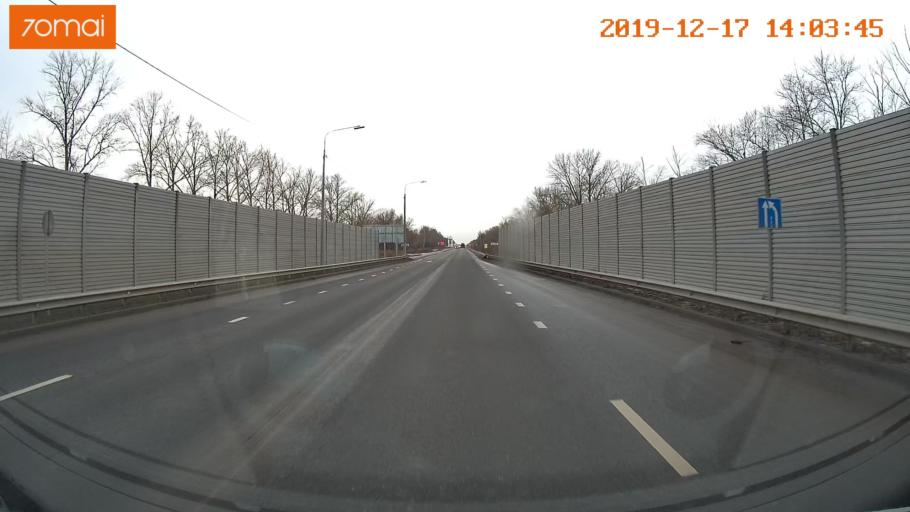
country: RU
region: Rjazan
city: Ryazan'
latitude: 54.6066
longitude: 39.6345
